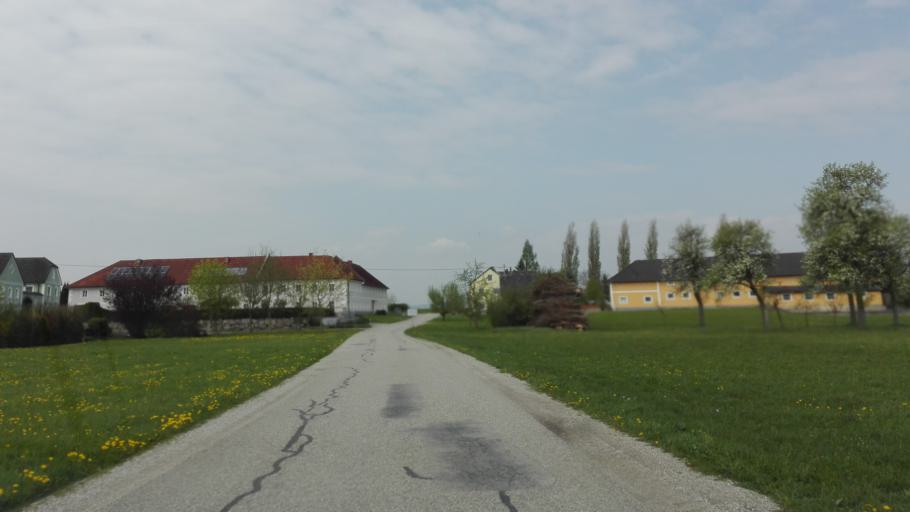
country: AT
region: Lower Austria
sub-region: Politischer Bezirk Amstetten
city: Strengberg
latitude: 48.1835
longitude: 14.6792
